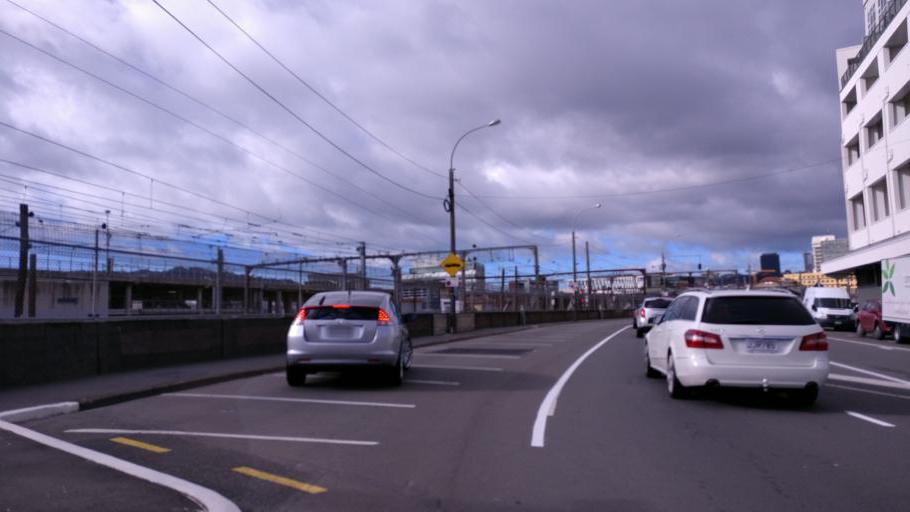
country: NZ
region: Wellington
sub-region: Wellington City
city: Wellington
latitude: -41.2746
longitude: 174.7837
